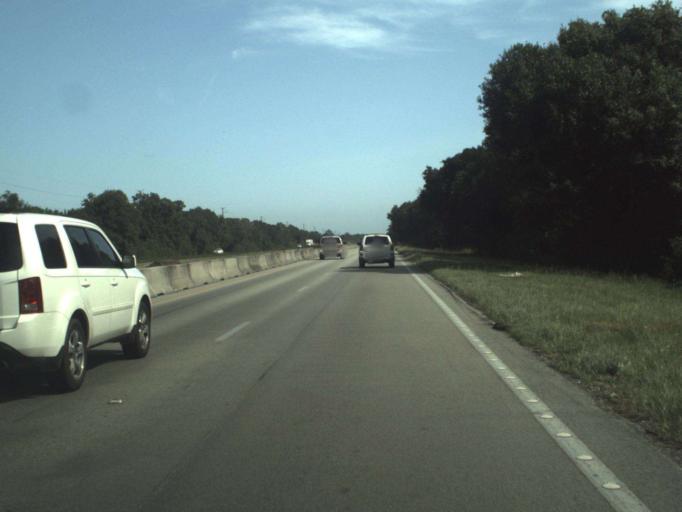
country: US
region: Florida
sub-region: Indian River County
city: West Vero Corridor
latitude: 27.6871
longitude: -80.5355
